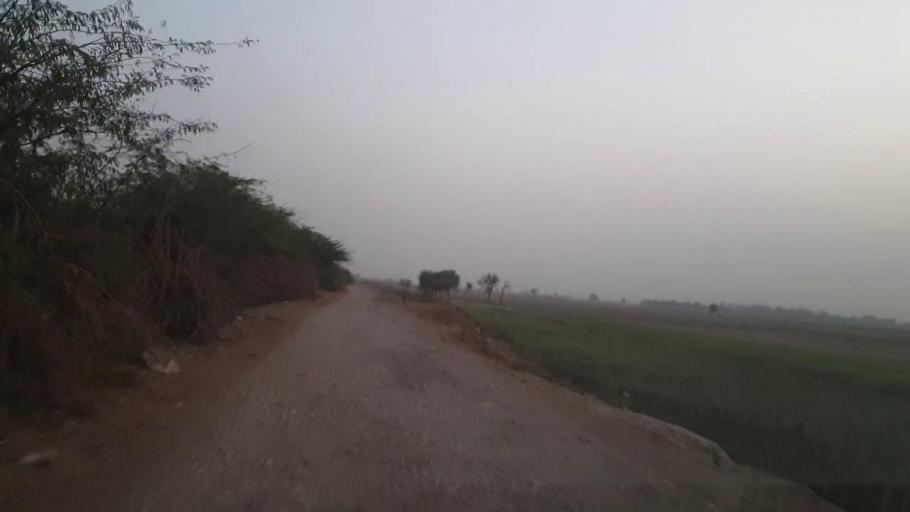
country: PK
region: Sindh
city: Nabisar
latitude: 25.0883
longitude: 69.5699
